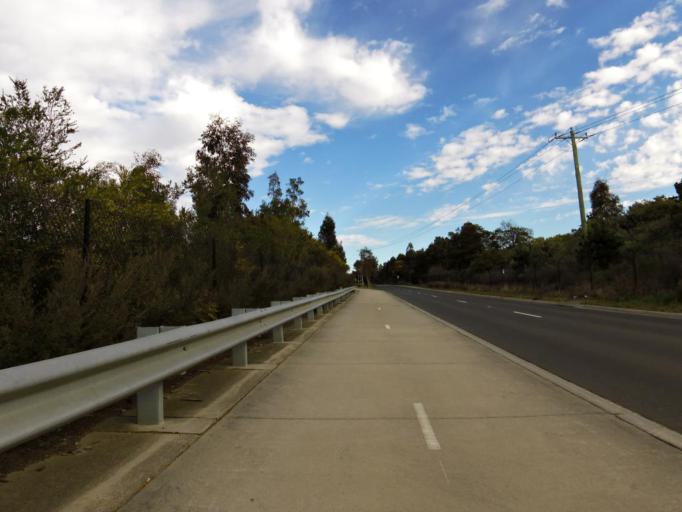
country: AU
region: Victoria
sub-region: Knox
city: Wantirna South
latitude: -37.8860
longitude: 145.2145
